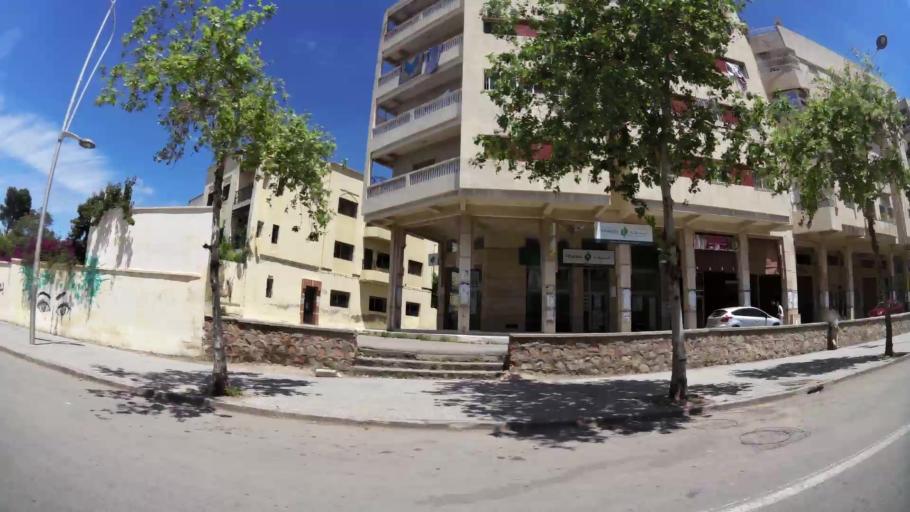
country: MA
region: Fes-Boulemane
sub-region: Fes
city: Fes
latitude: 34.0148
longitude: -4.9831
